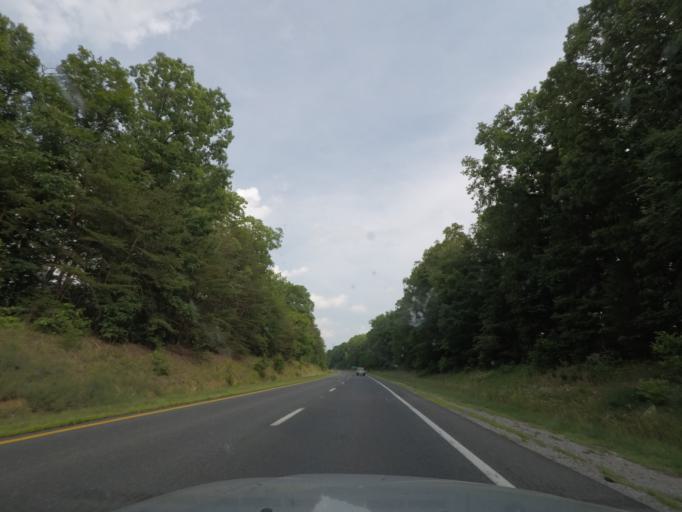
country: US
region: Virginia
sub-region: Prince Edward County
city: Farmville
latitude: 37.2725
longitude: -78.4175
